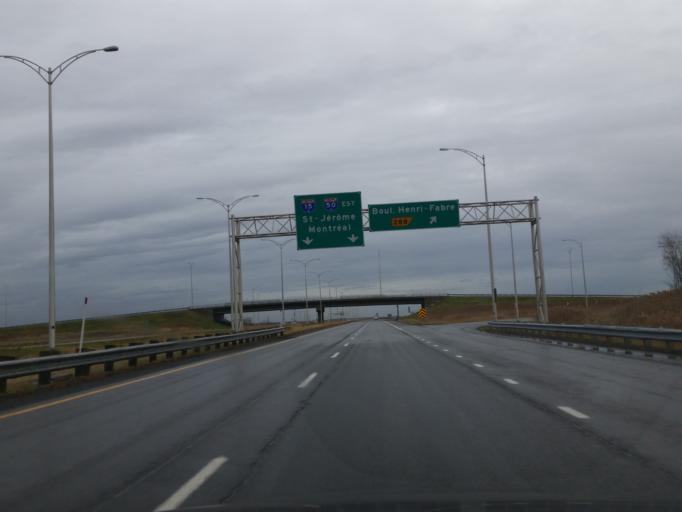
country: CA
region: Quebec
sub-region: Laurentides
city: Mirabel
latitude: 45.6964
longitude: -74.0141
